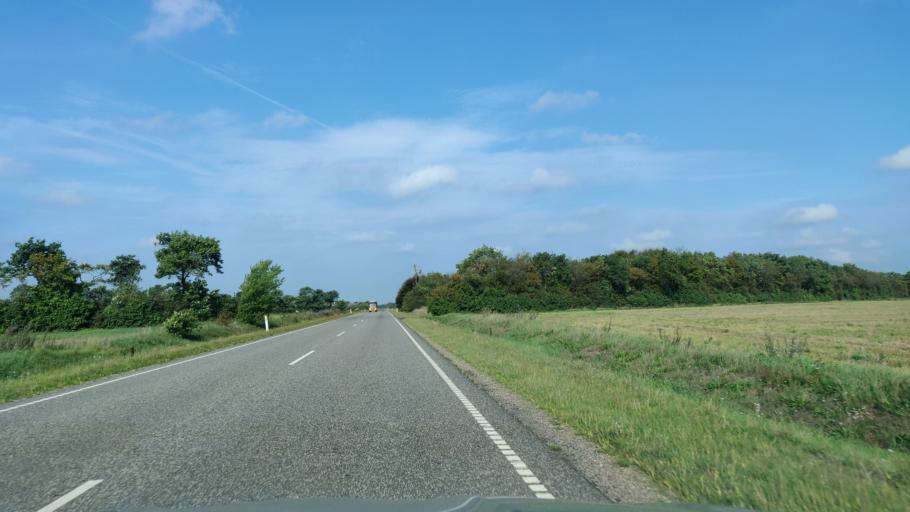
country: DK
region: Central Jutland
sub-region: Herning Kommune
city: Sunds
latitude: 56.2566
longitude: 9.0424
